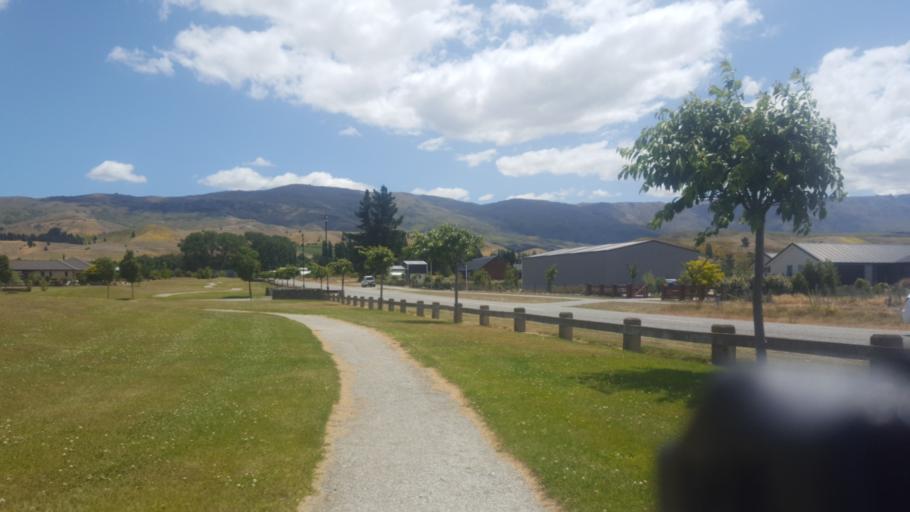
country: NZ
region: Otago
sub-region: Queenstown-Lakes District
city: Wanaka
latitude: -45.0310
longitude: 169.2033
